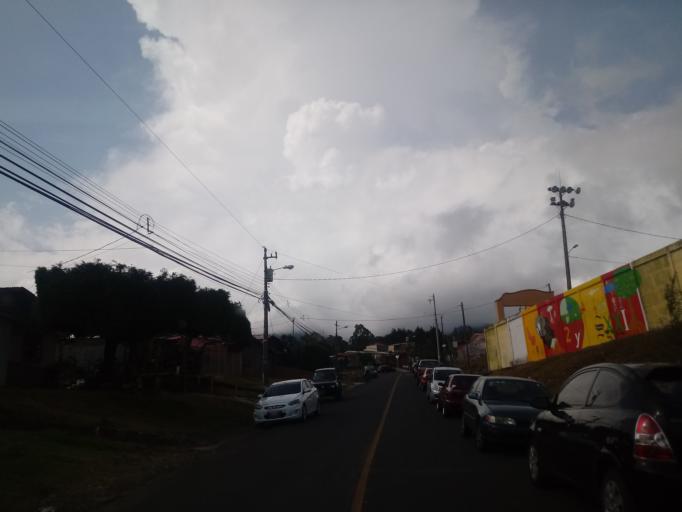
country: CR
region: Heredia
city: Angeles
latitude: 10.0255
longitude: -84.0474
